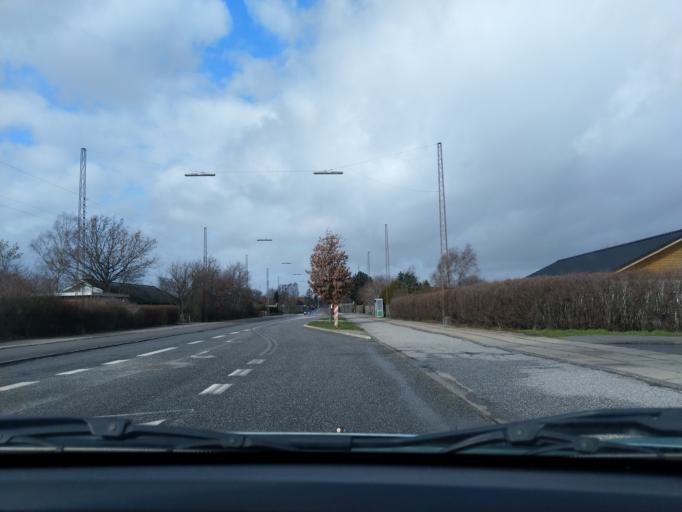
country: DK
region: Zealand
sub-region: Naestved Kommune
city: Naestved
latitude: 55.2153
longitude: 11.7711
